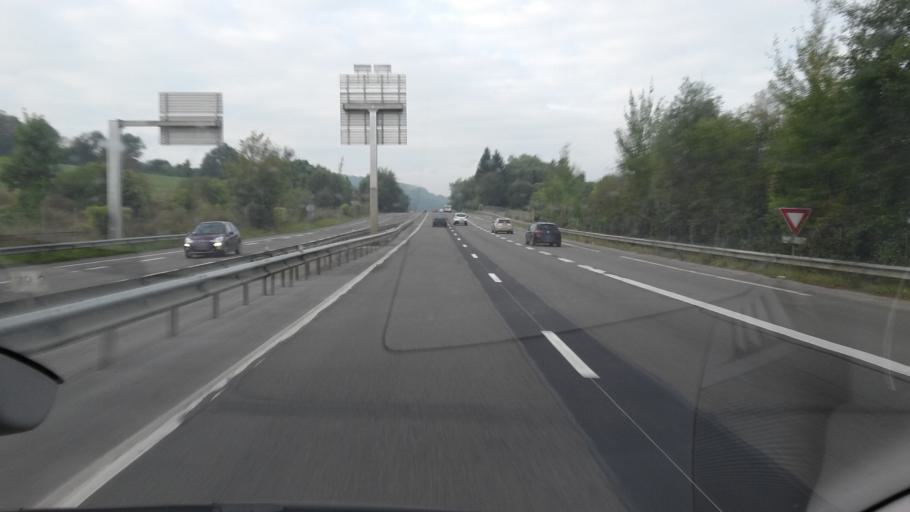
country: FR
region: Champagne-Ardenne
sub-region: Departement des Ardennes
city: La Francheville
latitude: 49.6917
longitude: 4.6777
